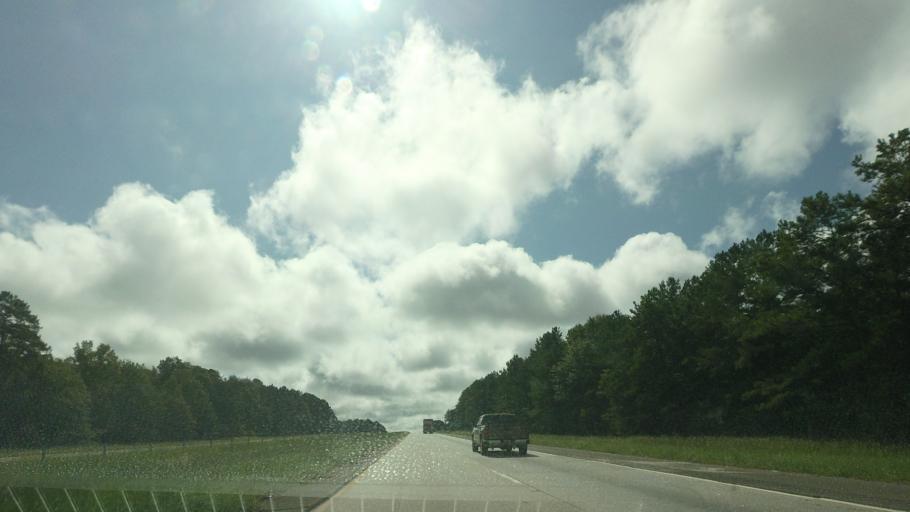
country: US
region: Georgia
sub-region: Twiggs County
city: Jeffersonville
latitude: 32.6618
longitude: -83.4544
